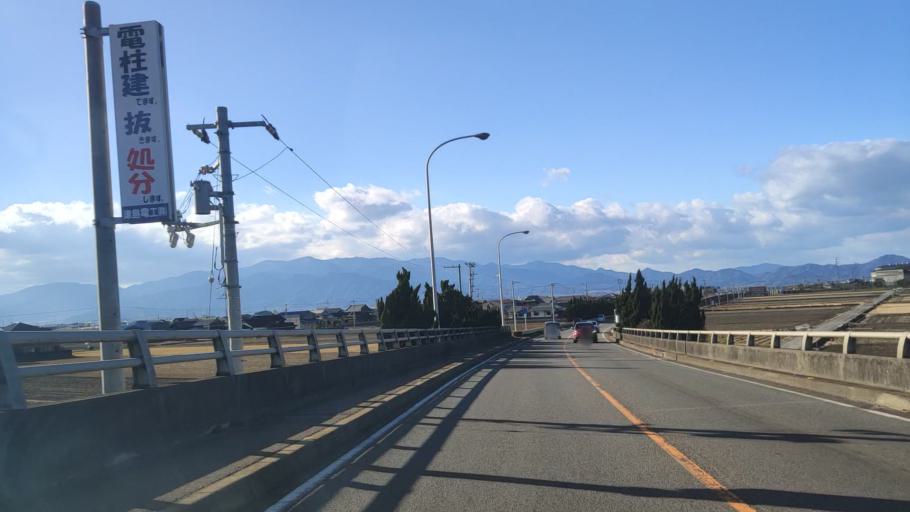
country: JP
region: Ehime
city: Saijo
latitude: 33.9160
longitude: 133.1312
